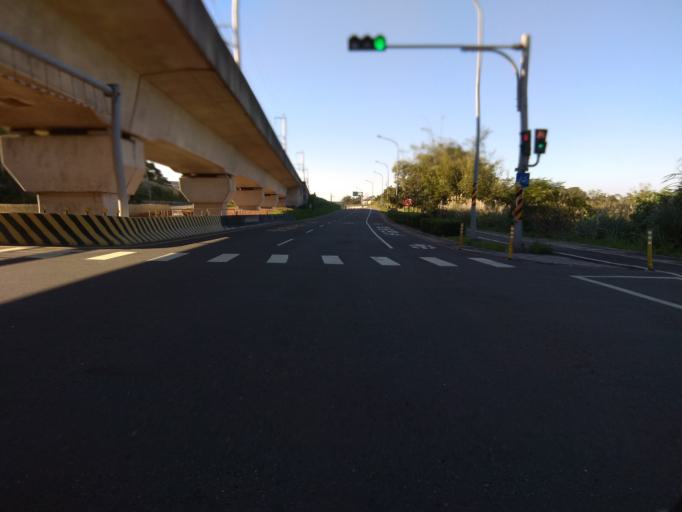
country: TW
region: Taiwan
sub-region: Hsinchu
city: Zhubei
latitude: 24.8933
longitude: 121.0768
